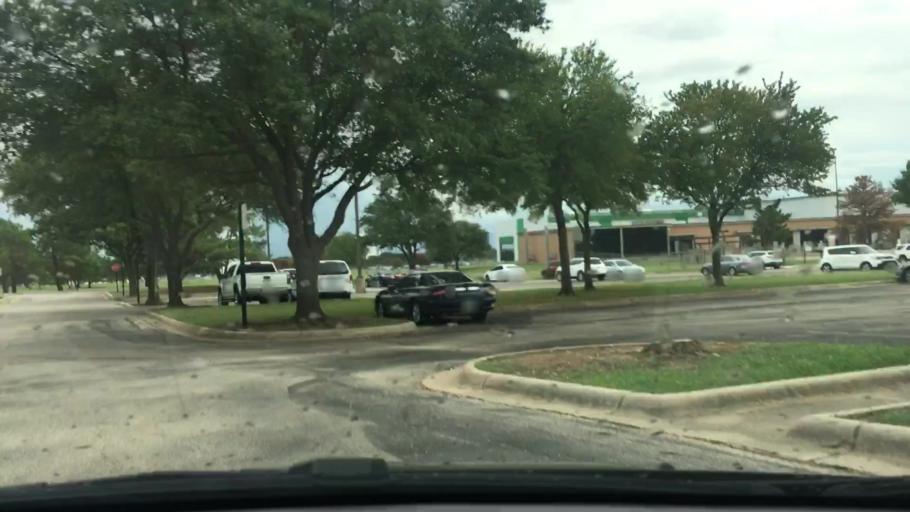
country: US
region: Texas
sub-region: Denton County
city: Denton
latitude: 33.2566
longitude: -97.1528
